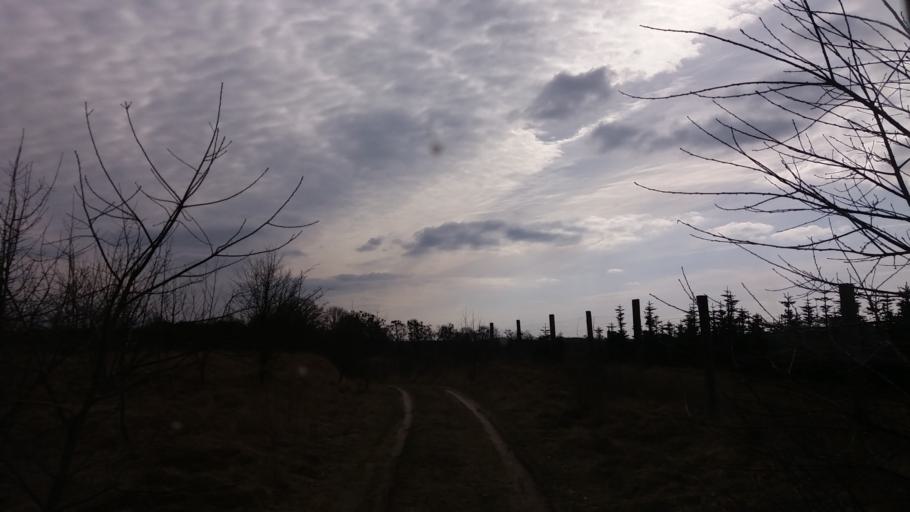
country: PL
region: West Pomeranian Voivodeship
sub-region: Powiat choszczenski
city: Bierzwnik
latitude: 53.1209
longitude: 15.6294
